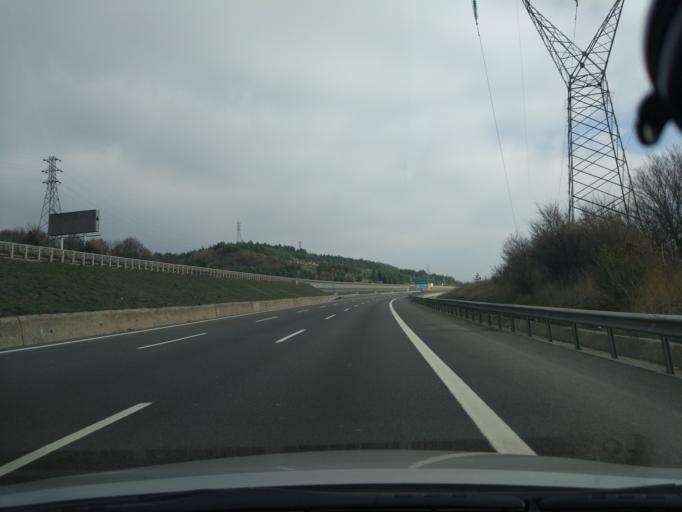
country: TR
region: Bolu
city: Bolu
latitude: 40.7308
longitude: 31.5172
